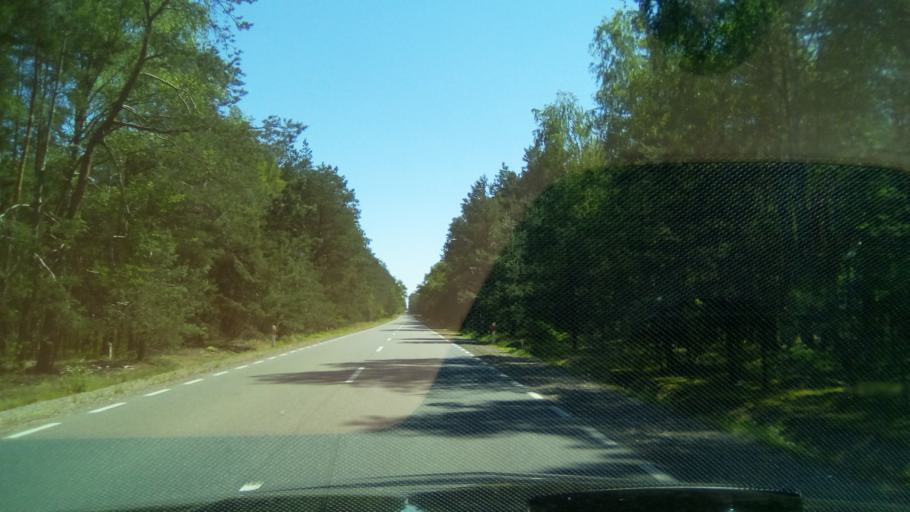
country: PL
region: Masovian Voivodeship
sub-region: Powiat przysuski
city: Odrzywol
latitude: 51.5228
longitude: 20.5760
